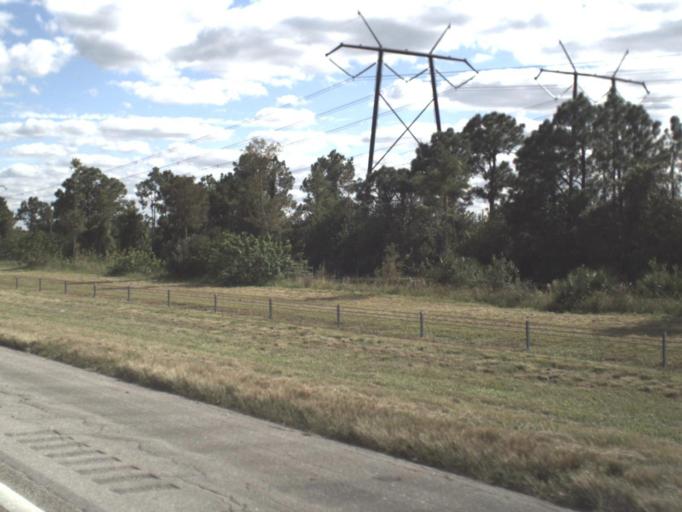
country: US
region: Florida
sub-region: Indian River County
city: West Vero Corridor
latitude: 27.5412
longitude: -80.6206
